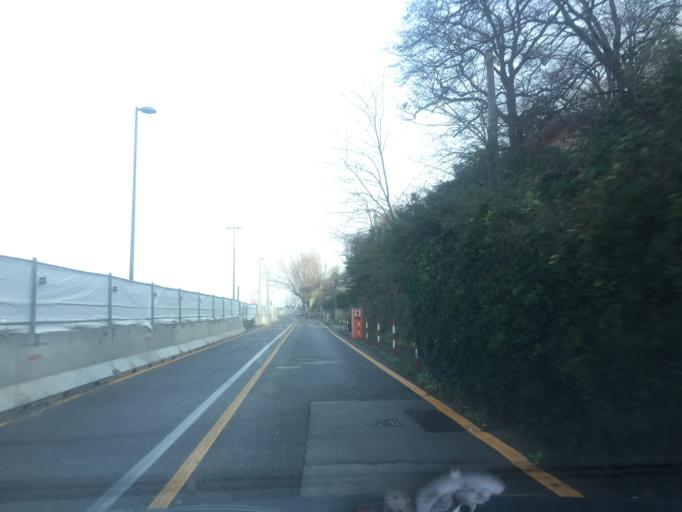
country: SI
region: Koper-Capodistria
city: Ankaran
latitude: 45.6073
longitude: 13.7302
